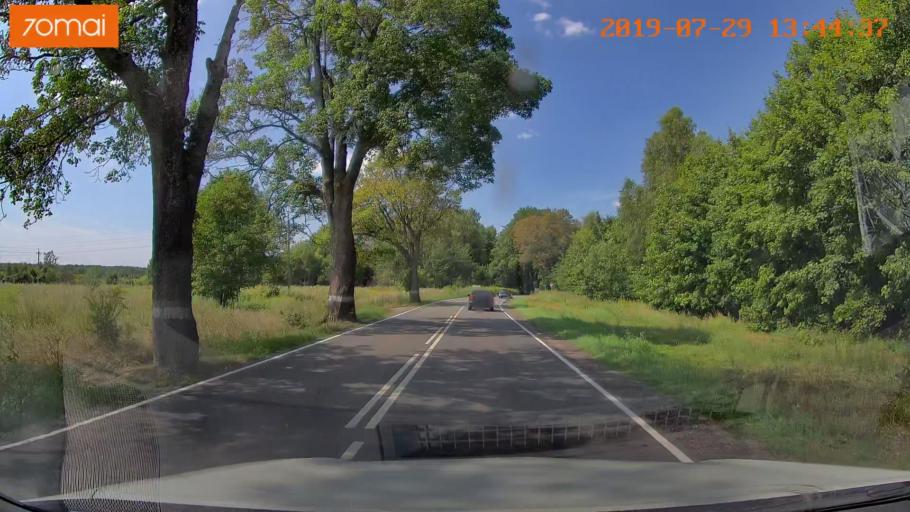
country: RU
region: Kaliningrad
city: Svetlyy
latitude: 54.7380
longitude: 20.0857
